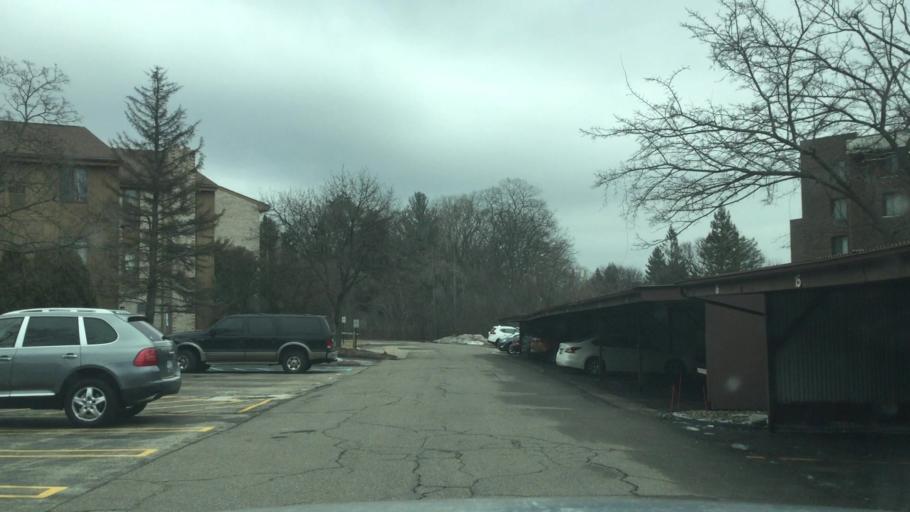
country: US
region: Michigan
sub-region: Oakland County
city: Franklin
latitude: 42.5042
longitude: -83.3082
